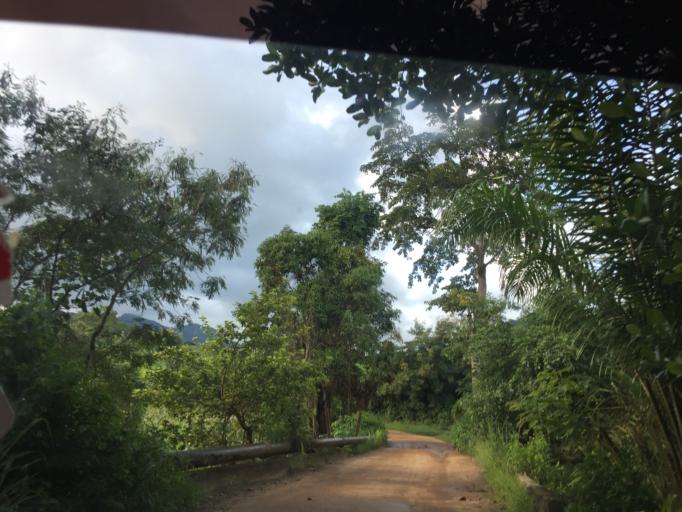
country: TZ
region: Tanga
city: Muheza
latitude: -5.1591
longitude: 38.7696
